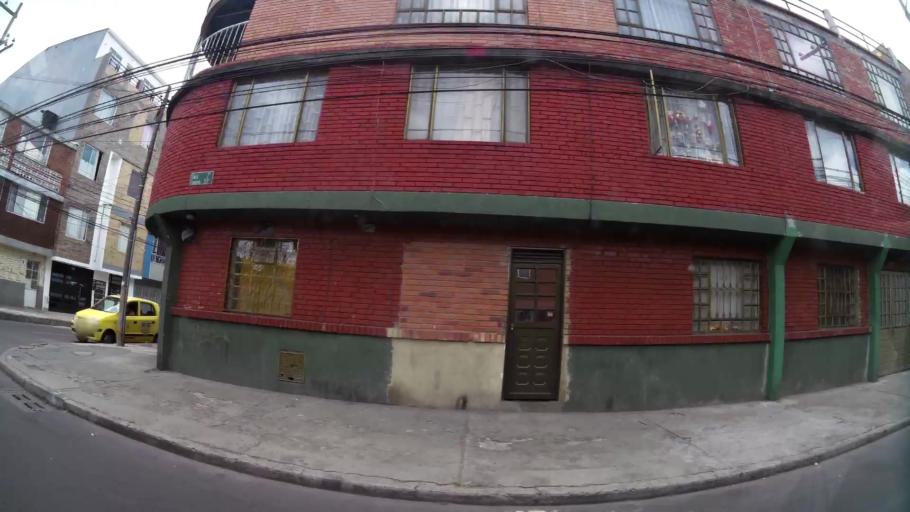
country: CO
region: Bogota D.C.
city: Bogota
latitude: 4.6161
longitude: -74.1201
